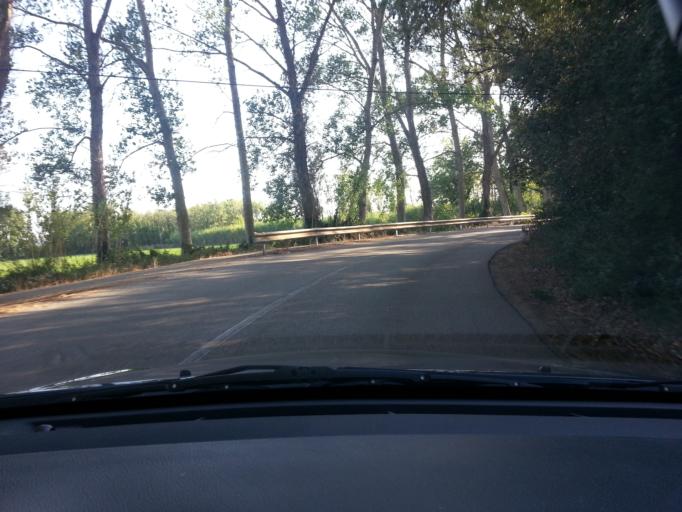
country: ES
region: Catalonia
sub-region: Provincia de Girona
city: Pals
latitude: 42.0122
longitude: 3.1669
